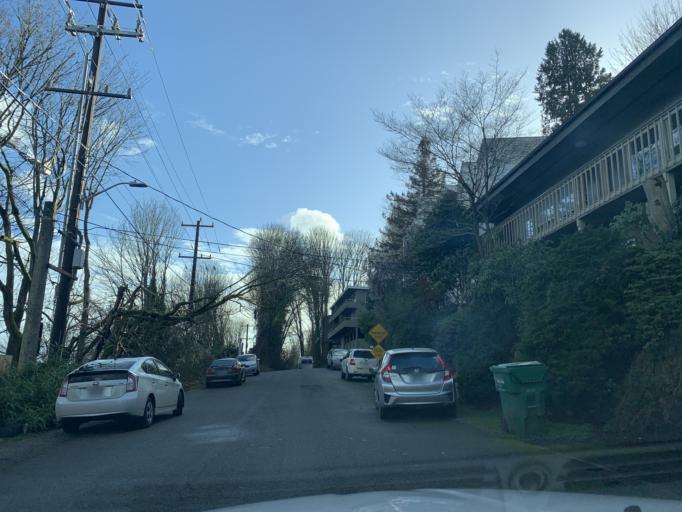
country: US
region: Washington
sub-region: King County
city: Seattle
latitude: 47.6642
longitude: -122.3034
